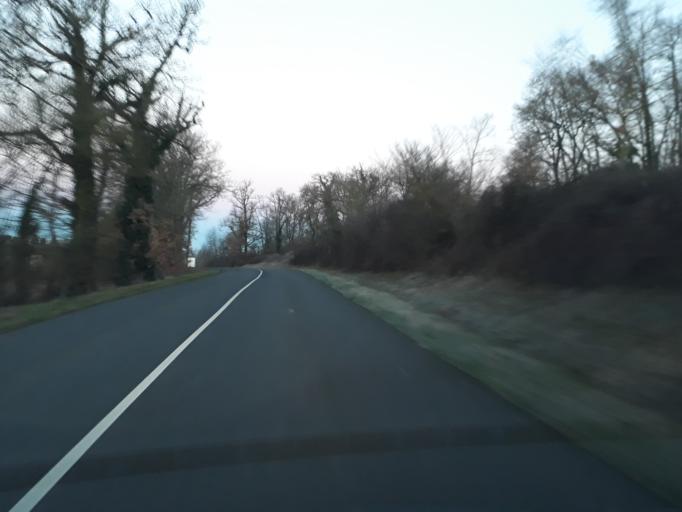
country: FR
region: Midi-Pyrenees
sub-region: Departement du Gers
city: Lombez
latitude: 43.5262
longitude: 0.8617
